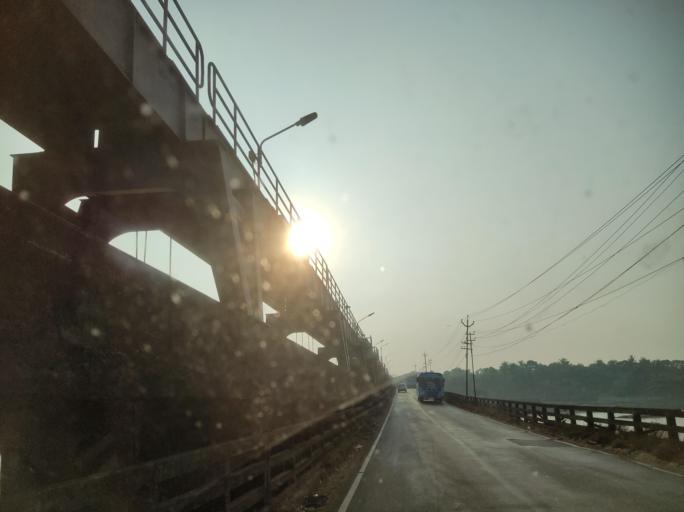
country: IN
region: Kerala
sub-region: Alappuzha
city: Shertallai
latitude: 9.6732
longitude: 76.4039
